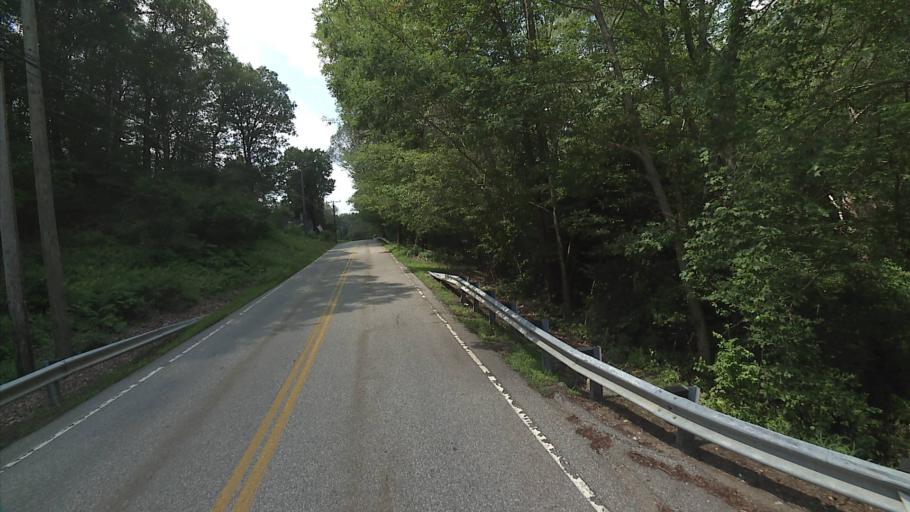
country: US
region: Connecticut
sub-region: New London County
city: Lisbon
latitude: 41.6153
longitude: -72.0286
